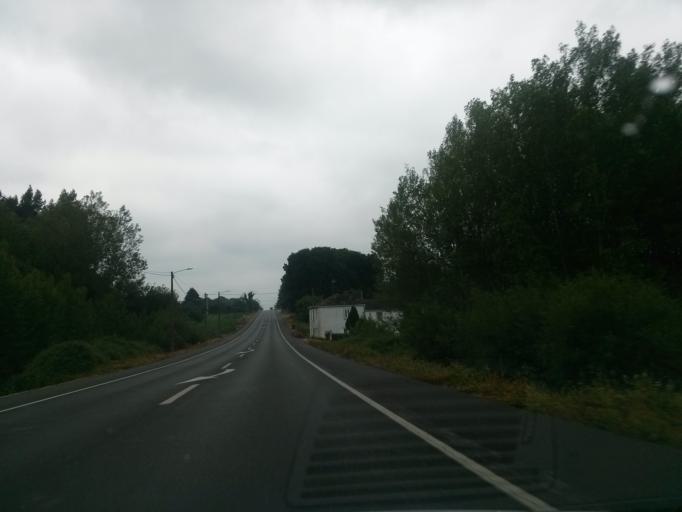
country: ES
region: Galicia
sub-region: Provincia de Lugo
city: Begonte
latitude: 43.1352
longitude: -7.6587
